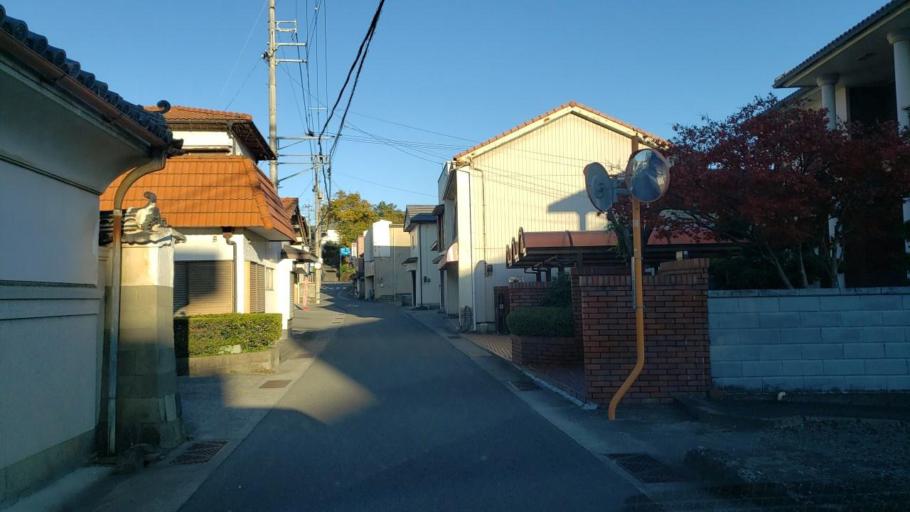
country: JP
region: Tokushima
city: Kamojimacho-jogejima
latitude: 34.0916
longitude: 134.2830
